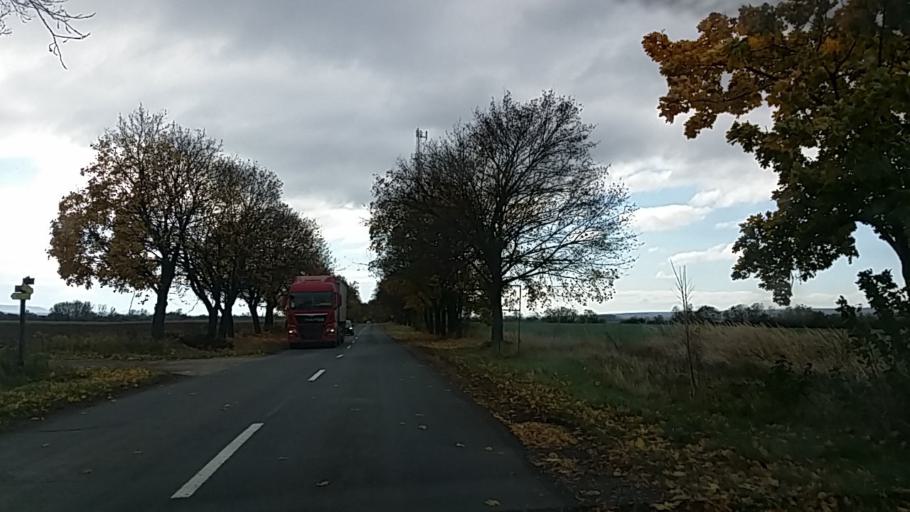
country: HU
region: Borsod-Abauj-Zemplen
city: Gonc
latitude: 48.4715
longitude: 21.2564
